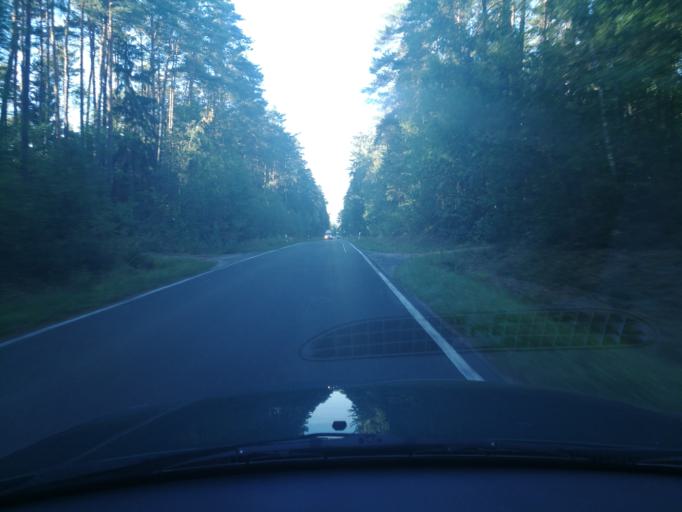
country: DE
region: Bavaria
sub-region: Regierungsbezirk Mittelfranken
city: Hessdorf
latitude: 49.6086
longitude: 10.9377
